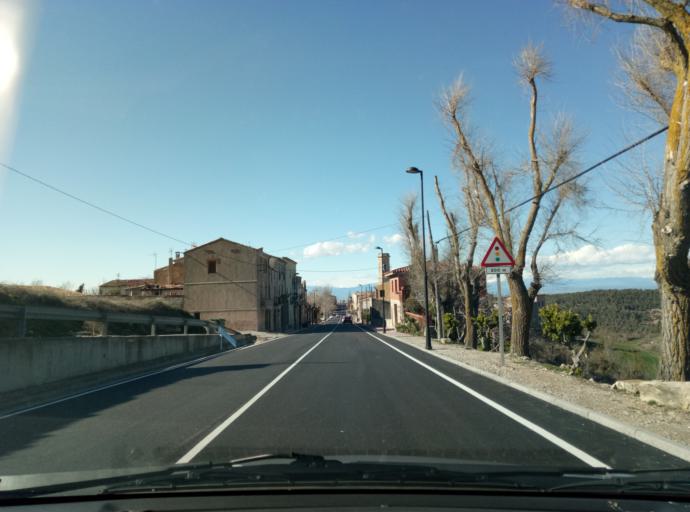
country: ES
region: Catalonia
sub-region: Provincia de Tarragona
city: Fores
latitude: 41.5026
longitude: 1.1871
